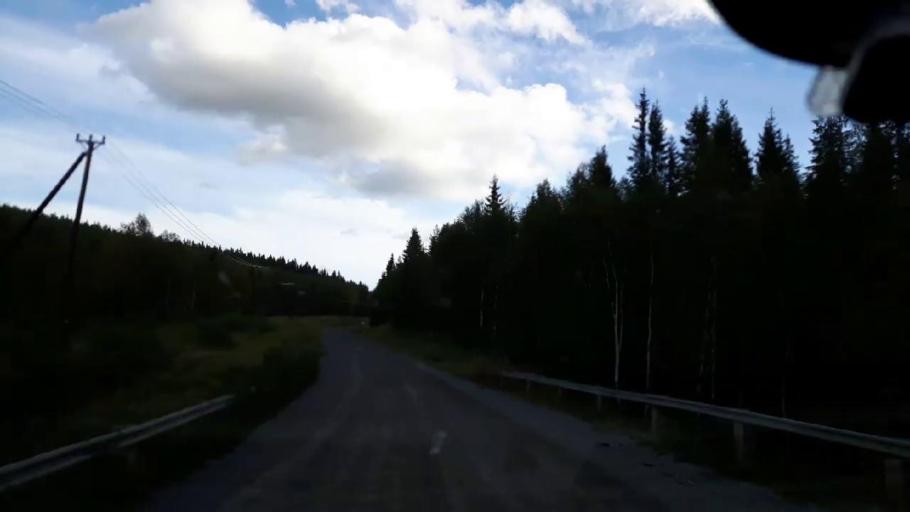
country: SE
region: Jaemtland
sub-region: Ragunda Kommun
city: Hammarstrand
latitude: 63.4195
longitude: 16.0725
